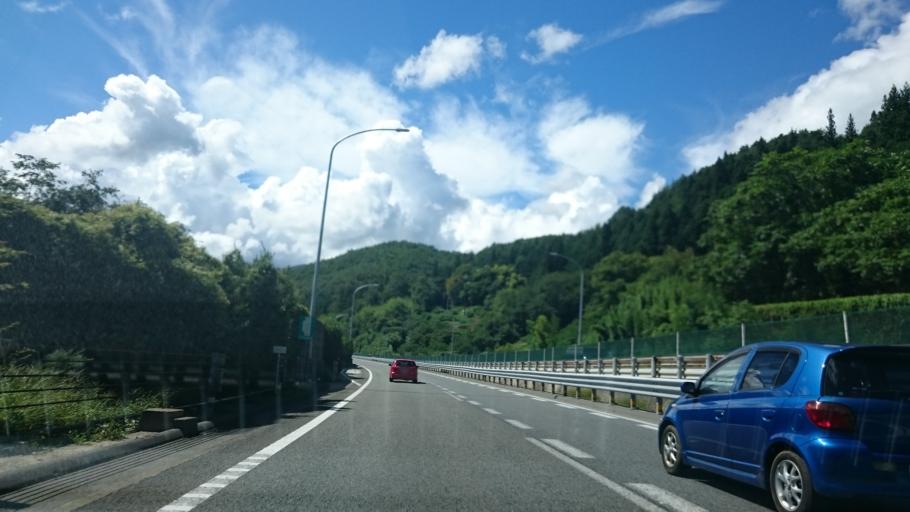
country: JP
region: Nagano
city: Iida
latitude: 35.4482
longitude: 137.7359
